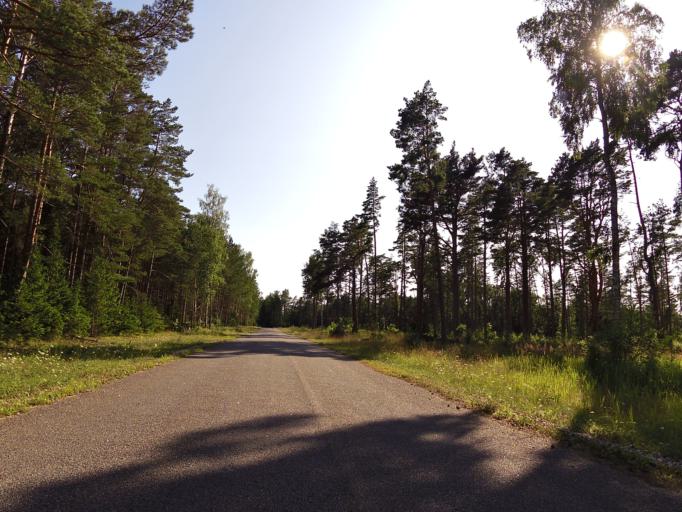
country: EE
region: Hiiumaa
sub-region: Kaerdla linn
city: Kardla
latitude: 58.8966
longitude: 22.2767
